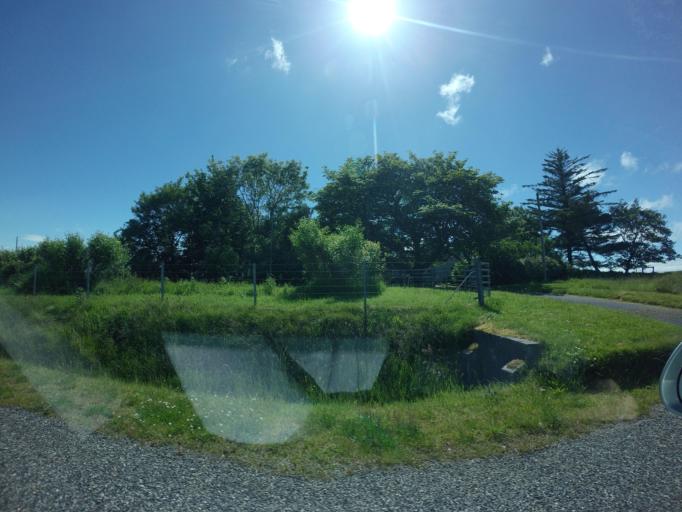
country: GB
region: Scotland
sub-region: Eilean Siar
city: Harris
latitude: 58.1926
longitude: -6.7109
